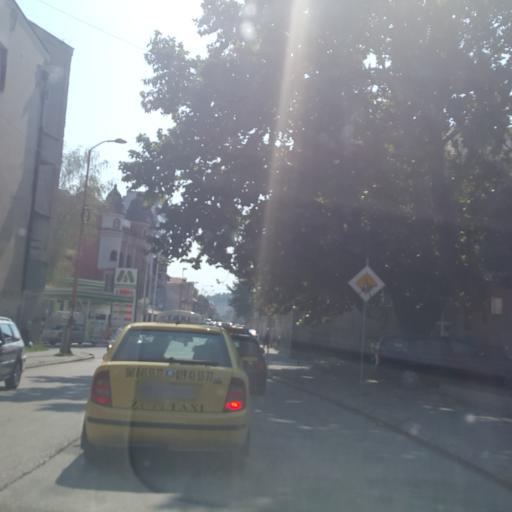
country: RS
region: Central Serbia
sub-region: Zajecarski Okrug
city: Zajecar
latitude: 43.9054
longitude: 22.2787
